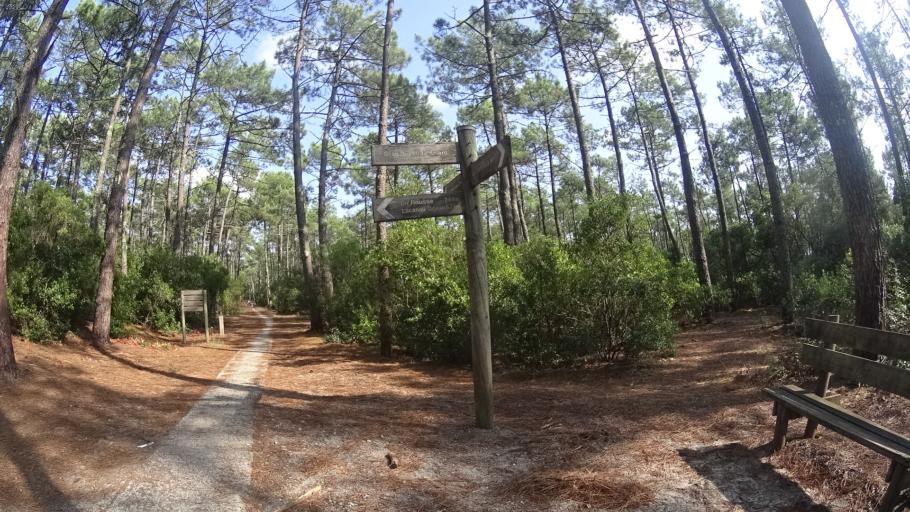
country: FR
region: Aquitaine
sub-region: Departement de la Gironde
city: Lacanau
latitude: 44.9632
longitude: -1.1726
